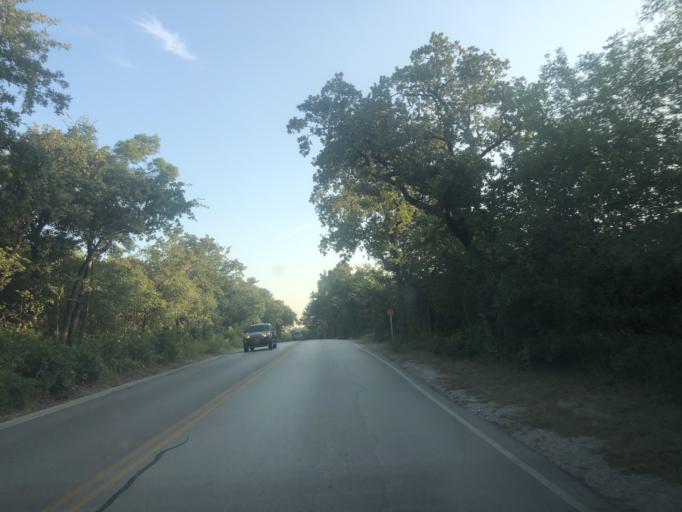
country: US
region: Texas
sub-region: Tarrant County
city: Lakeside
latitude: 32.7965
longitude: -97.4938
